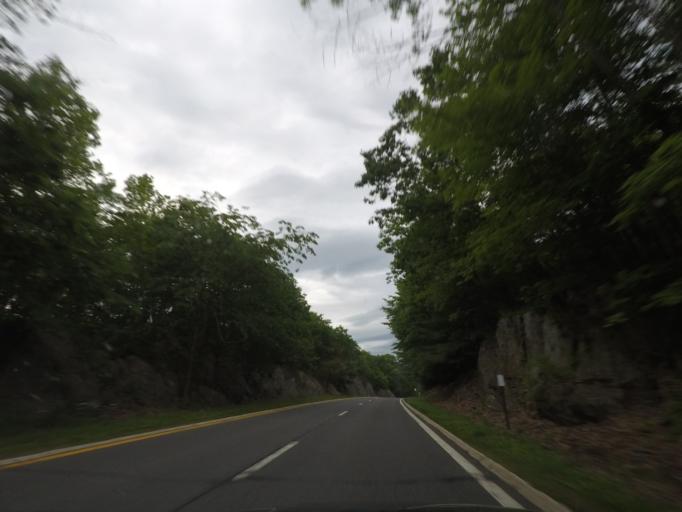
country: US
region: New York
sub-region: Dutchess County
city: Pine Plains
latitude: 42.0416
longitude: -73.7338
